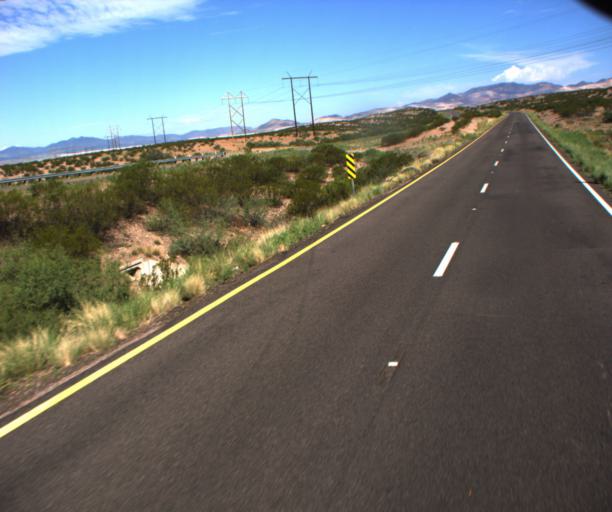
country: US
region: Arizona
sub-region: Greenlee County
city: Clifton
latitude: 32.9871
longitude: -109.2654
